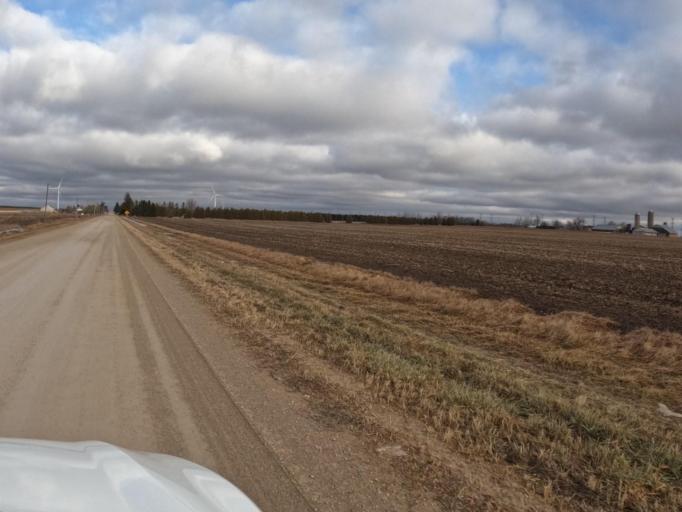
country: CA
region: Ontario
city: Shelburne
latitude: 43.8862
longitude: -80.3592
